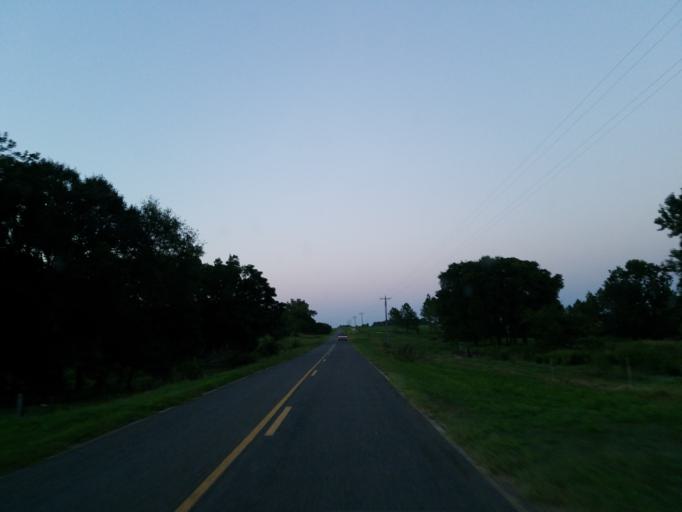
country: US
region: Georgia
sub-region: Dooly County
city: Unadilla
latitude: 32.2822
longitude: -83.7944
